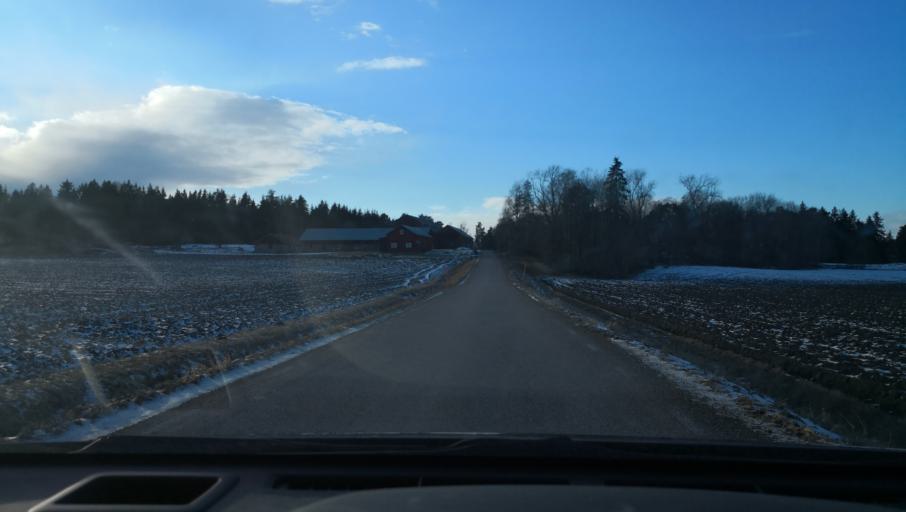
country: SE
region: Uppsala
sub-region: Enkopings Kommun
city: Irsta
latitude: 59.6578
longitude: 16.7945
